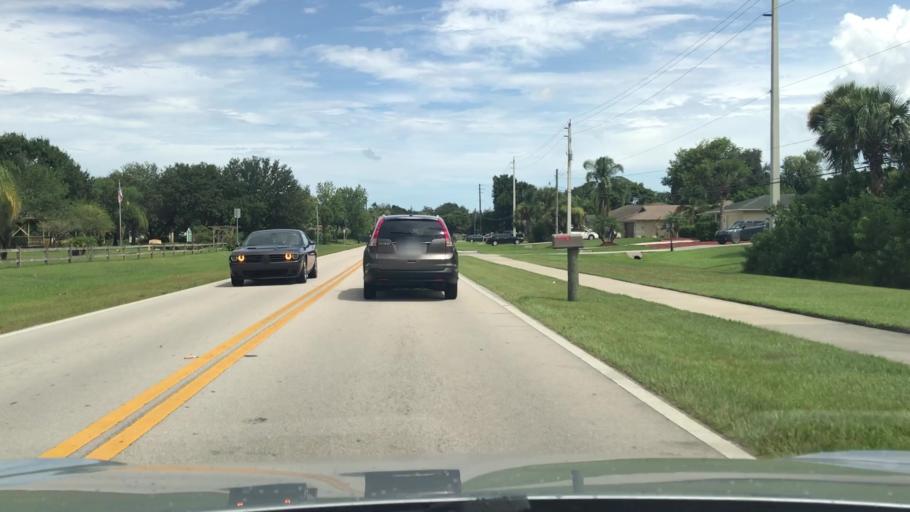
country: US
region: Florida
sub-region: Indian River County
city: Sebastian
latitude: 27.7821
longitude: -80.4902
